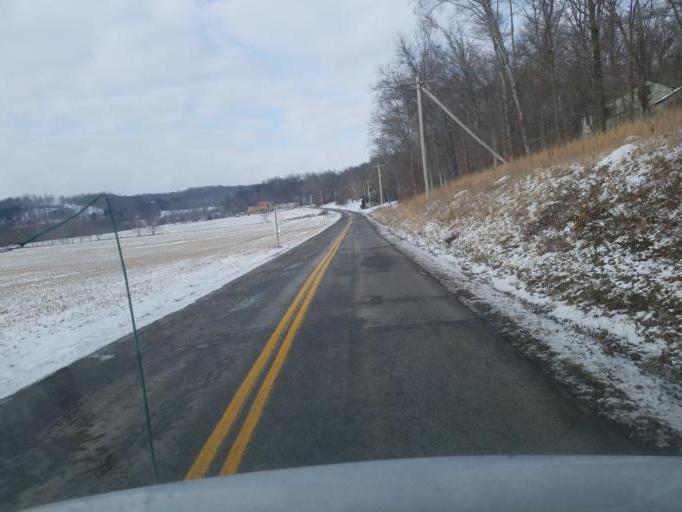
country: US
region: Ohio
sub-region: Holmes County
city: Millersburg
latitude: 40.4543
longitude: -81.9049
